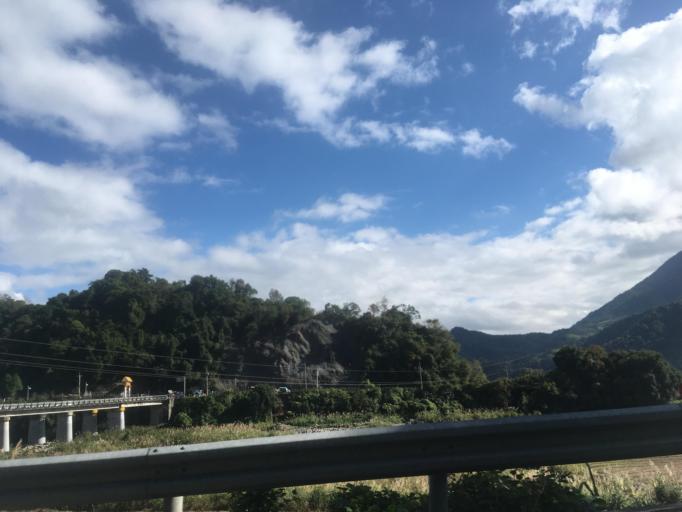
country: TW
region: Taiwan
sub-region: Yilan
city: Yilan
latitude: 24.6095
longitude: 121.5257
